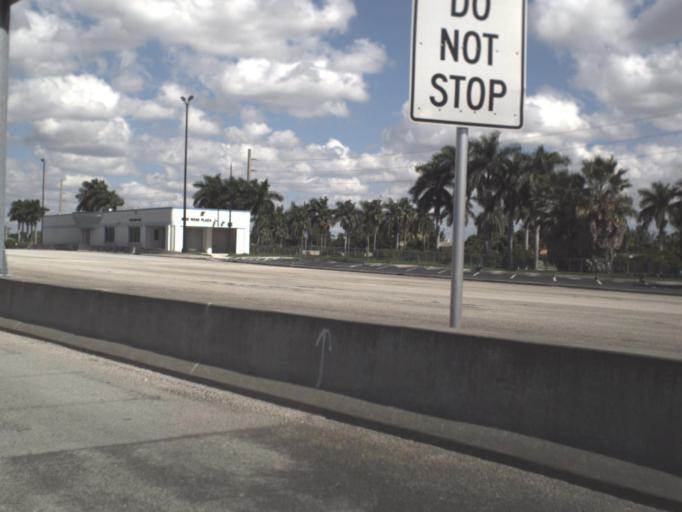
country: US
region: Florida
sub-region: Miami-Dade County
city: Westwood Lake
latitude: 25.7192
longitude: -80.3838
